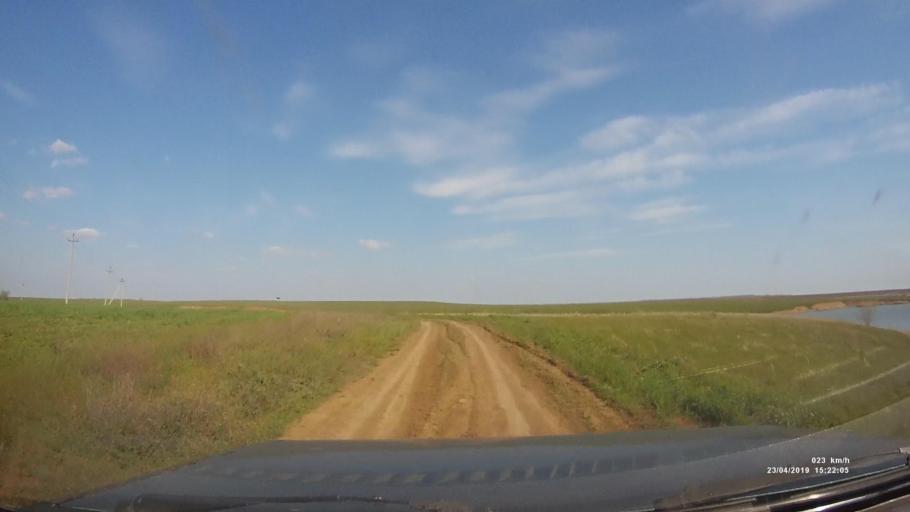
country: RU
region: Rostov
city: Remontnoye
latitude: 46.5281
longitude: 42.9679
